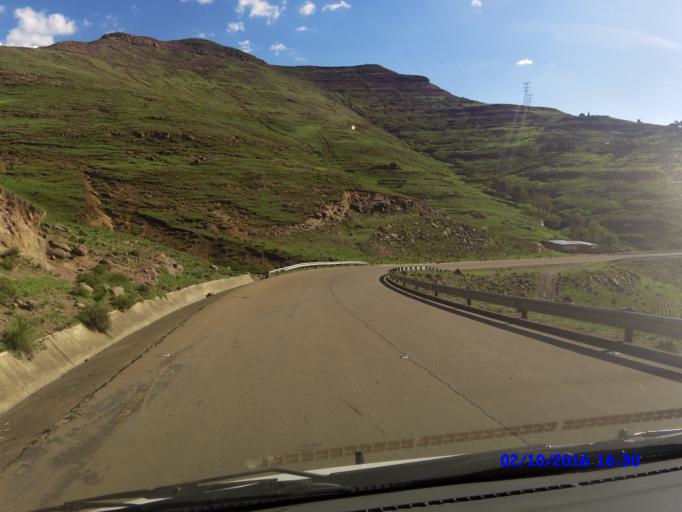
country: LS
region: Maseru
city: Nako
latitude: -29.4807
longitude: 28.0790
